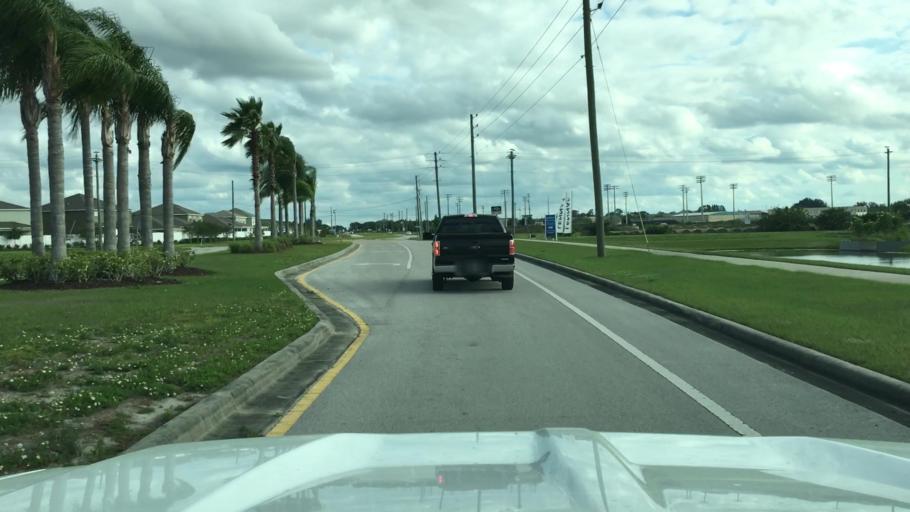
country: US
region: Florida
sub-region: Hillsborough County
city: Ruskin
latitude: 27.7287
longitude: -82.4021
